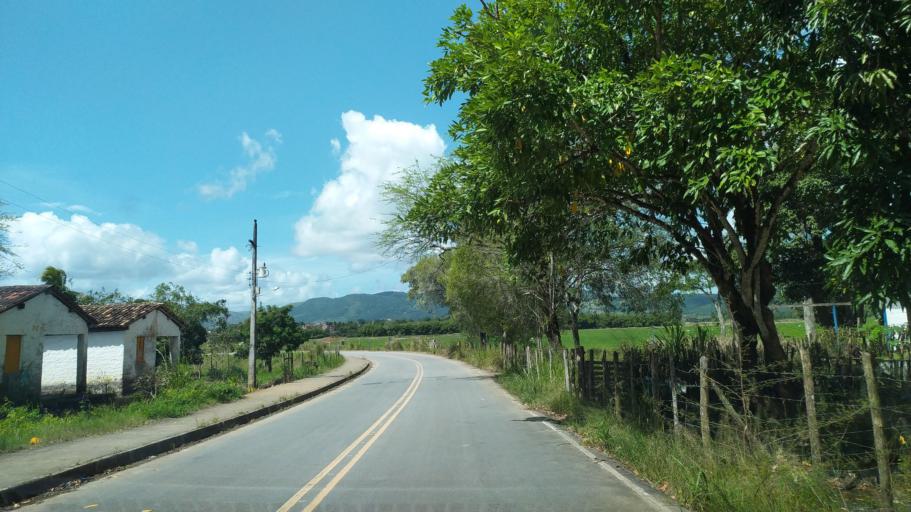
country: BR
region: Alagoas
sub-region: Uniao Dos Palmares
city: Uniao dos Palmares
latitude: -9.1632
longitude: -36.0490
